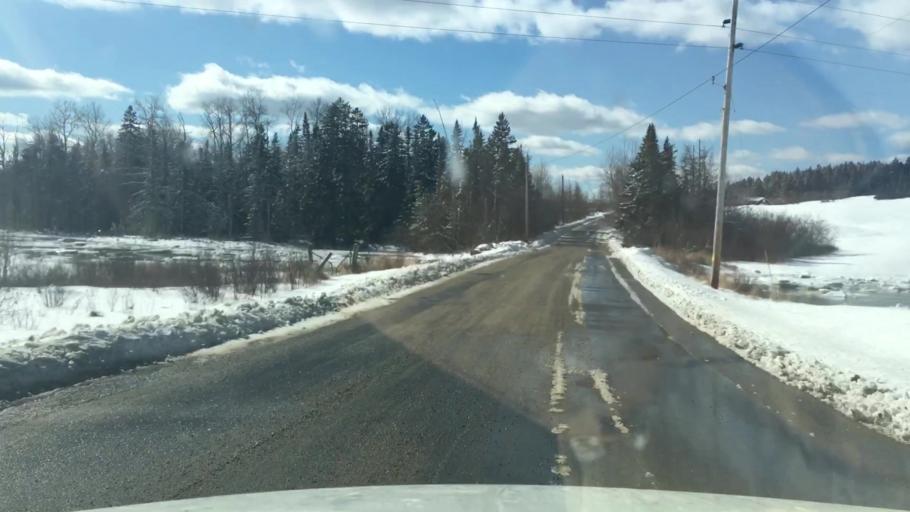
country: US
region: Maine
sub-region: Washington County
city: Machiasport
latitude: 44.6706
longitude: -67.4241
